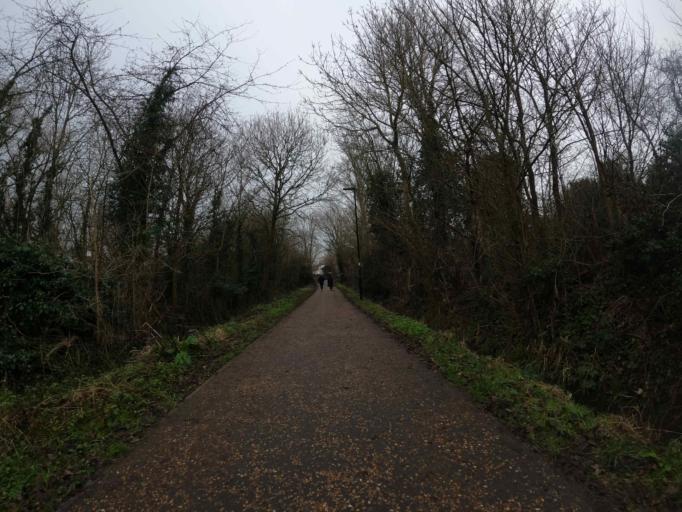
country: GB
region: England
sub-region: Greater London
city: Greenford
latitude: 51.5178
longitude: -0.3461
